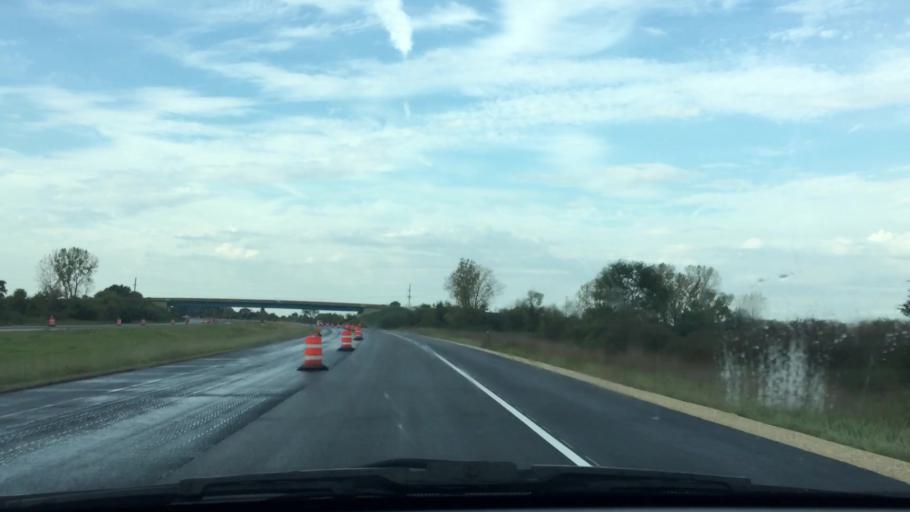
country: US
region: Illinois
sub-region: Whiteside County
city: Erie
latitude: 41.7060
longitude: -90.0513
